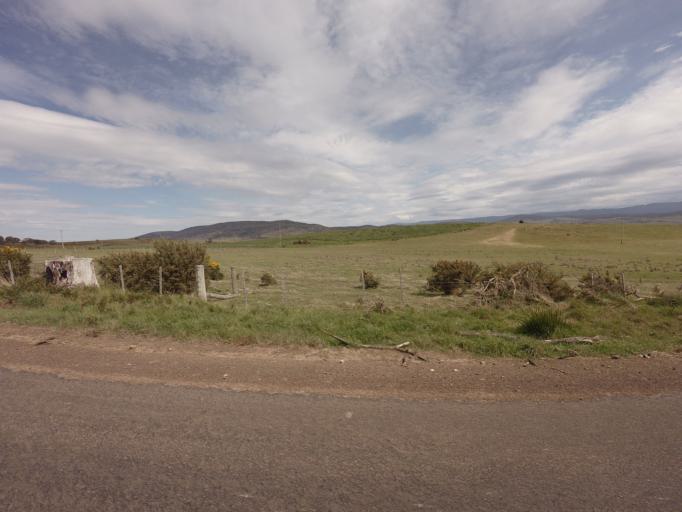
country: AU
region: Tasmania
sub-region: Northern Midlands
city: Evandale
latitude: -41.8934
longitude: 147.4047
